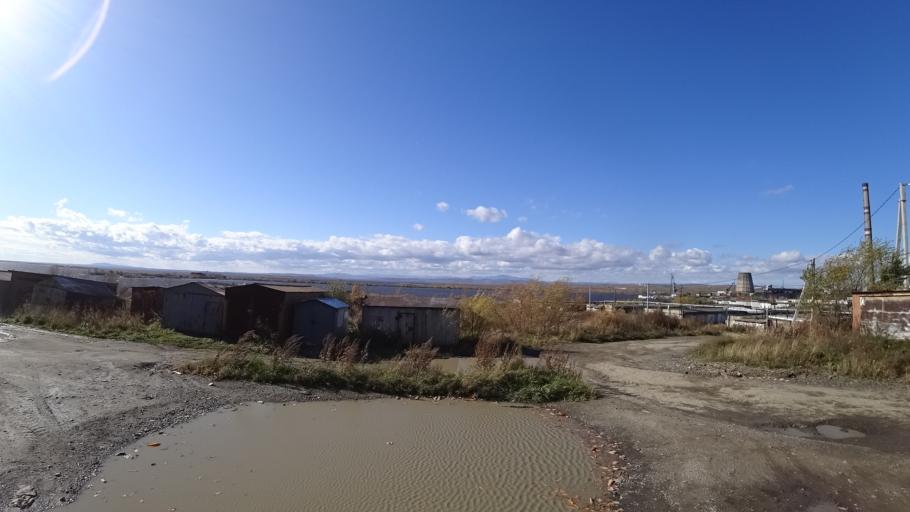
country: RU
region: Khabarovsk Krai
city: Amursk
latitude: 50.2166
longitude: 136.8891
